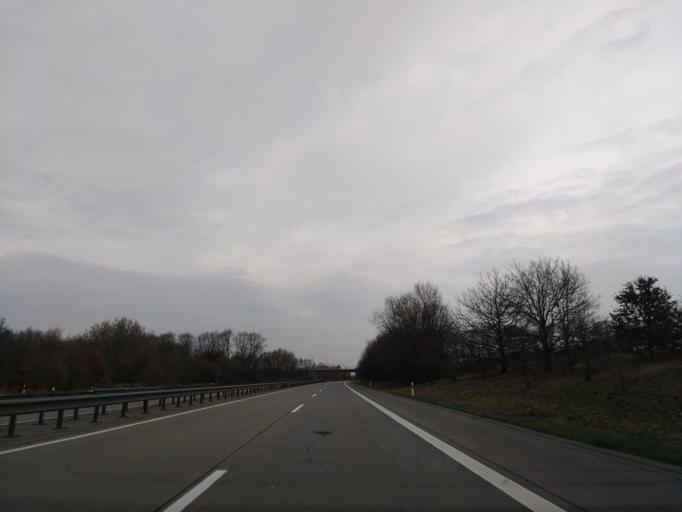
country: DE
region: Lower Saxony
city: Midlum
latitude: 53.7265
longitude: 8.6620
